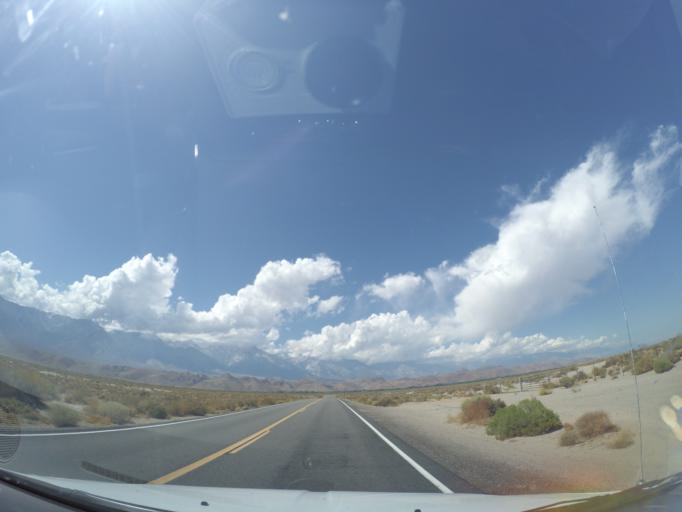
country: US
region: California
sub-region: Inyo County
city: Lone Pine
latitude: 36.5759
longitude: -118.0212
